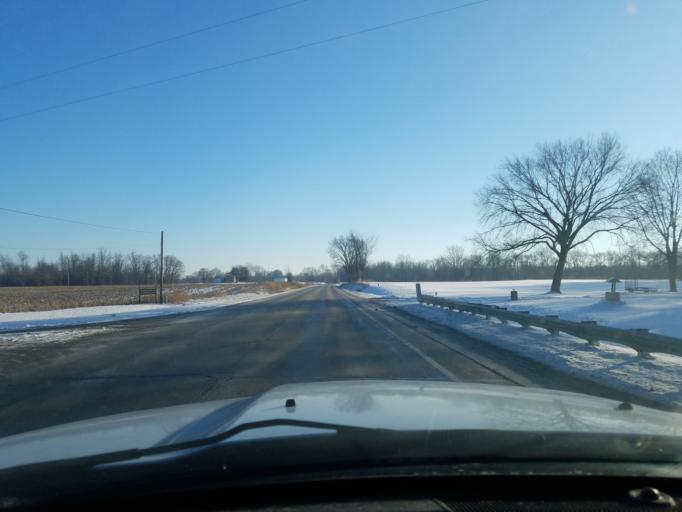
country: US
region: Indiana
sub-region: Noble County
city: Ligonier
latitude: 41.4581
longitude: -85.5222
